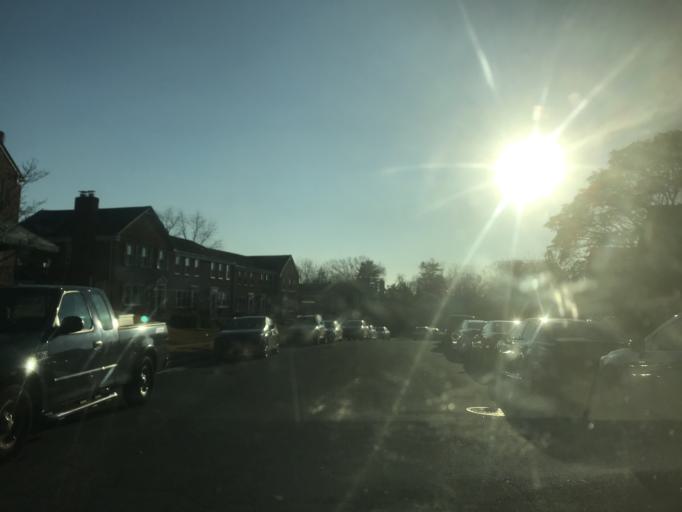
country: US
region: Maryland
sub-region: Baltimore County
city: Towson
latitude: 39.3911
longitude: -76.5749
